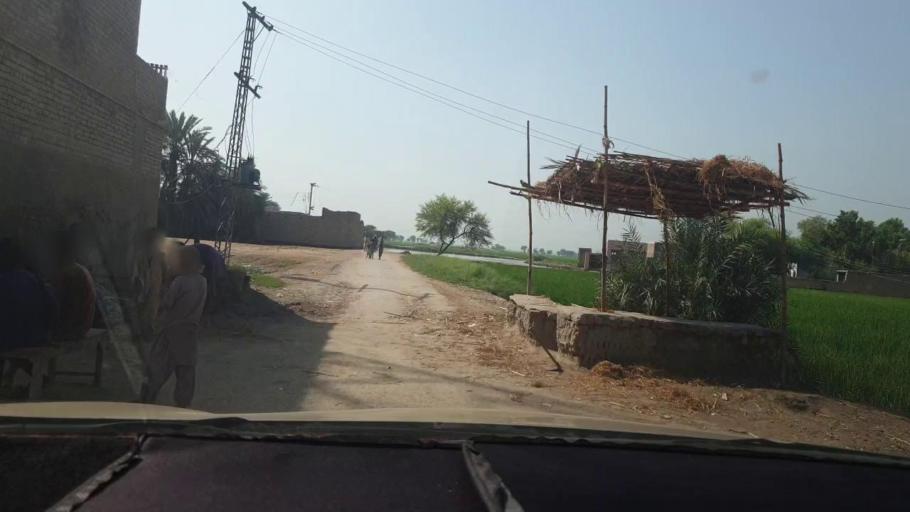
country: PK
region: Sindh
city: Kambar
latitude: 27.5592
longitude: 68.0592
